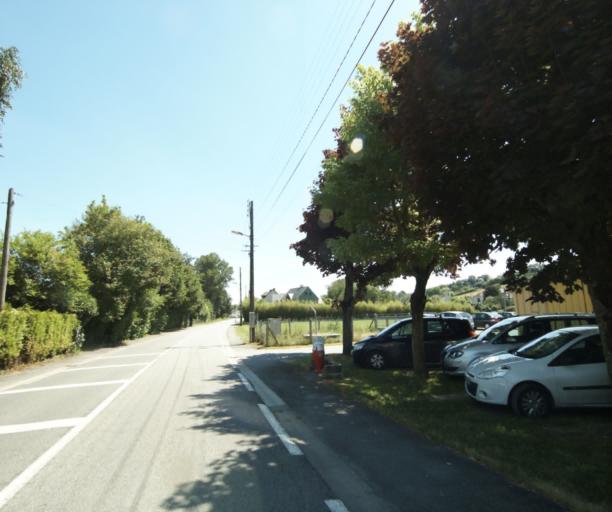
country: FR
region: Pays de la Loire
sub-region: Departement de la Mayenne
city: Laval
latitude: 48.0865
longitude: -0.7721
